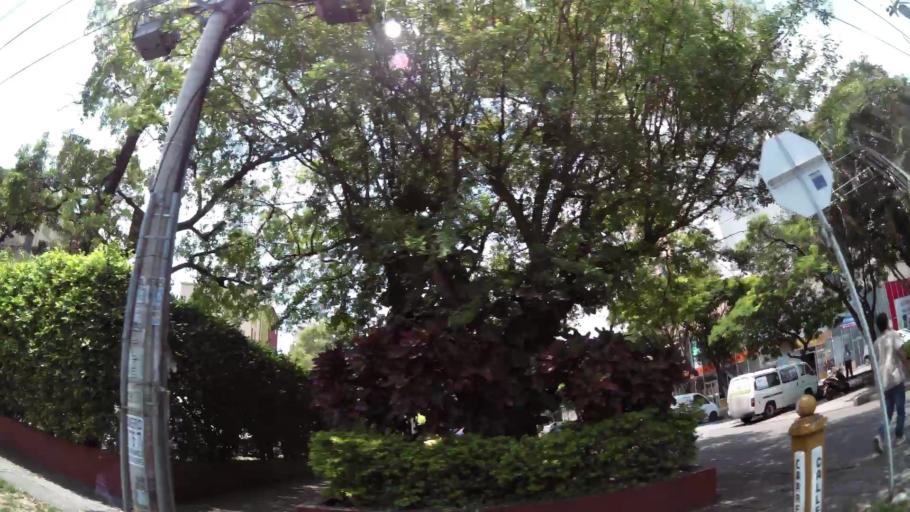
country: CO
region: Valle del Cauca
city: Cali
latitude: 3.4020
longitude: -76.5319
